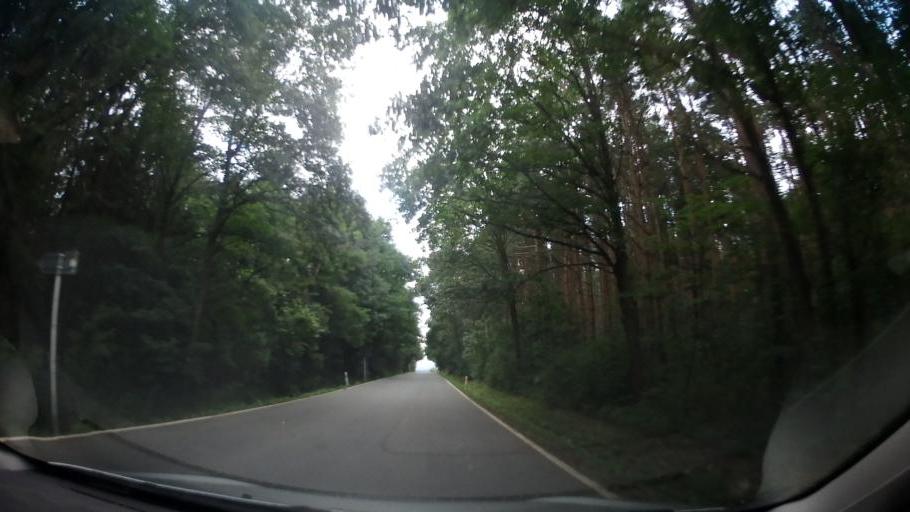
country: CZ
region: Olomoucky
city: Bila Lhota
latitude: 49.6846
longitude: 16.9953
